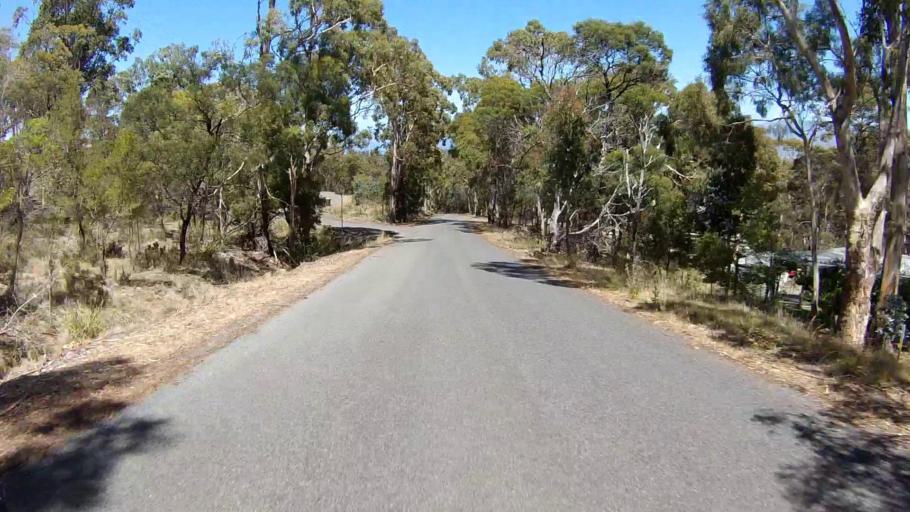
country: AU
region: Tasmania
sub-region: Clarence
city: Cambridge
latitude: -42.8488
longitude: 147.4309
